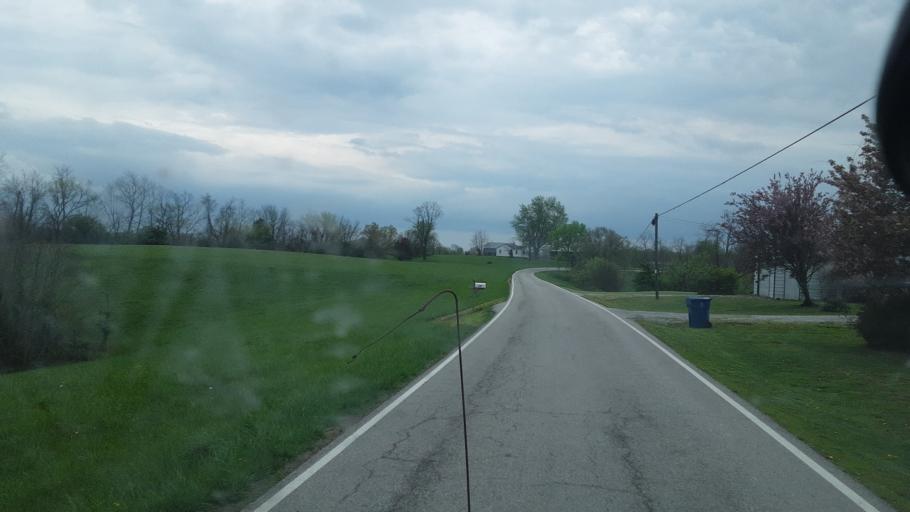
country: US
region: Kentucky
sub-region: Owen County
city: Owenton
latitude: 38.6560
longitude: -84.7718
